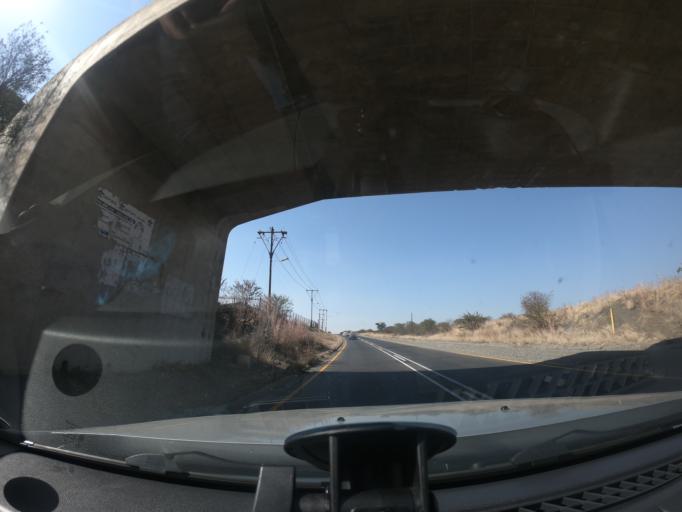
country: ZA
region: KwaZulu-Natal
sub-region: uThukela District Municipality
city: Ladysmith
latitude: -28.5432
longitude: 29.8081
